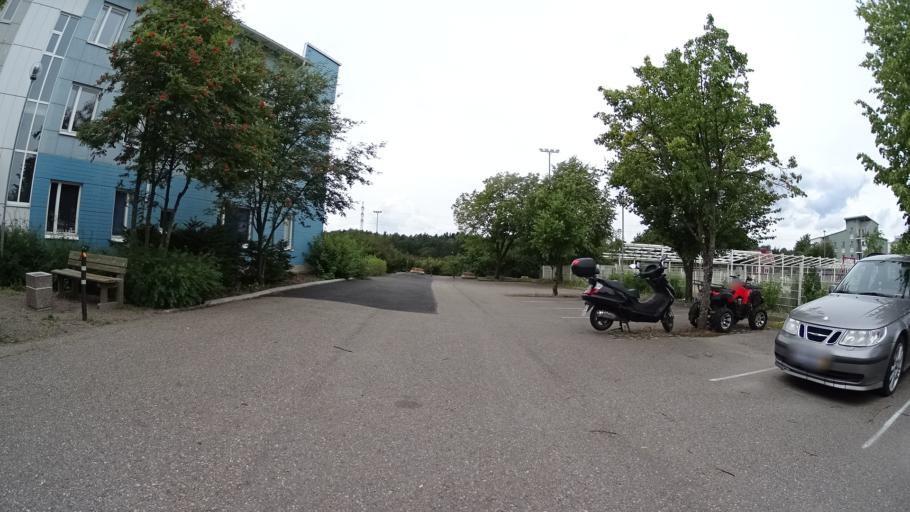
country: FI
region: Uusimaa
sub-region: Helsinki
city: Helsinki
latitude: 60.2010
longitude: 24.8943
